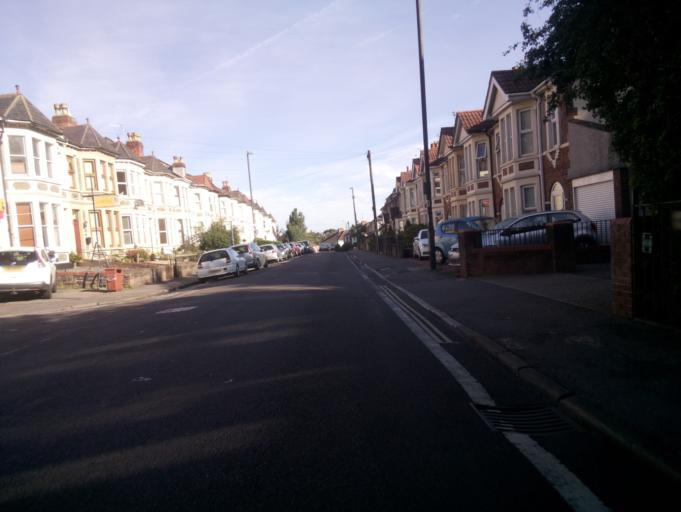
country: GB
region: England
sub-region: South Gloucestershire
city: Kingswood
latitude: 51.4504
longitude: -2.5471
